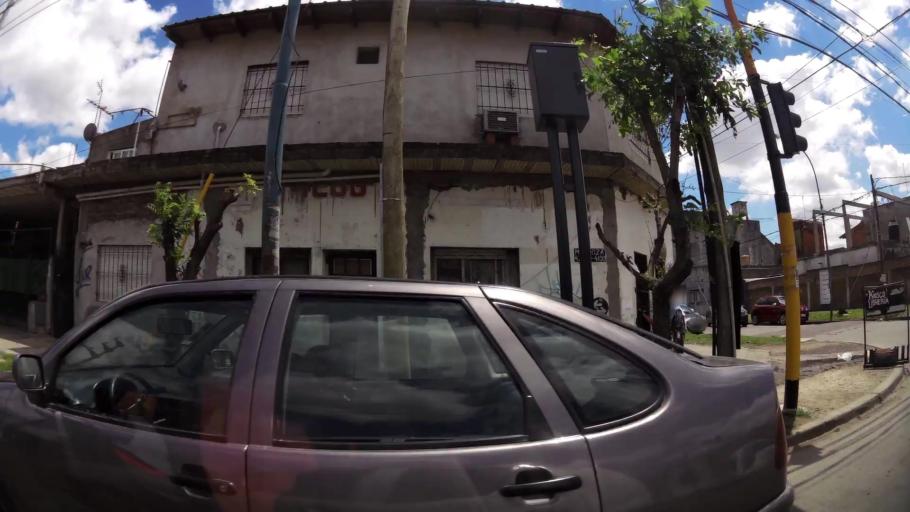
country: AR
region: Buenos Aires
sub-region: Partido de Lanus
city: Lanus
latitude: -34.7031
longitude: -58.4295
